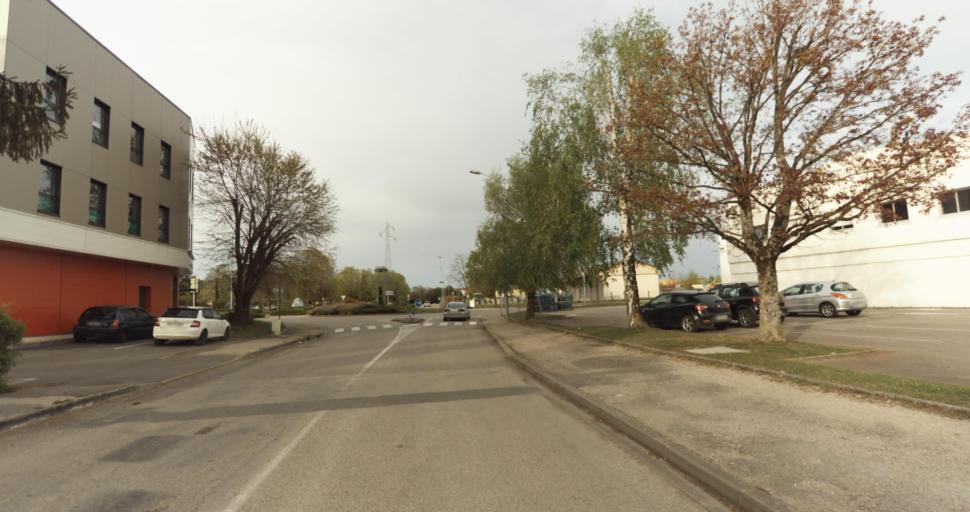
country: FR
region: Rhone-Alpes
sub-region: Departement de l'Ain
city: Amberieu-en-Bugey
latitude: 45.9631
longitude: 5.3445
